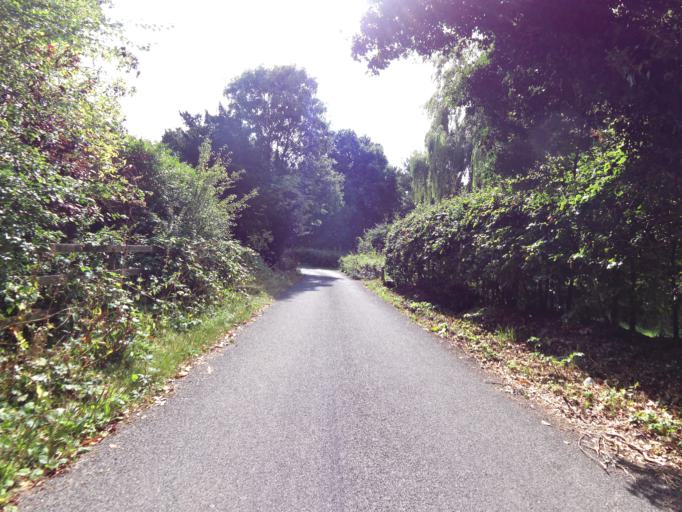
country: GB
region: England
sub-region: Hertfordshire
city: Shenley AV
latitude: 51.6959
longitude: -0.2551
